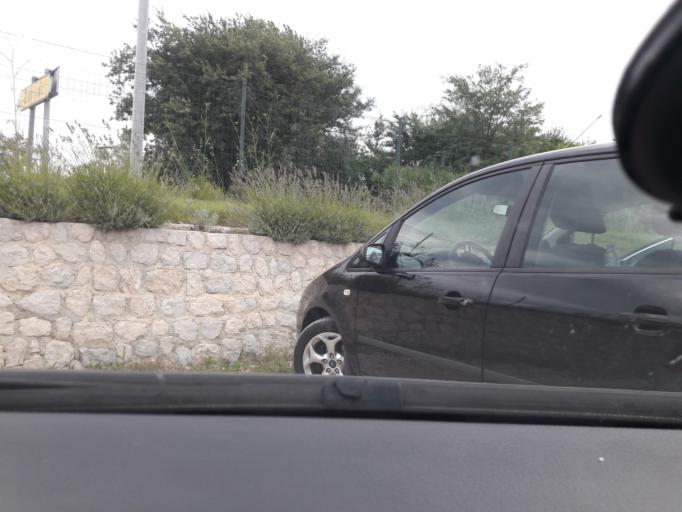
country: HR
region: Zadarska
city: Nin
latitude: 44.2438
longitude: 15.1924
